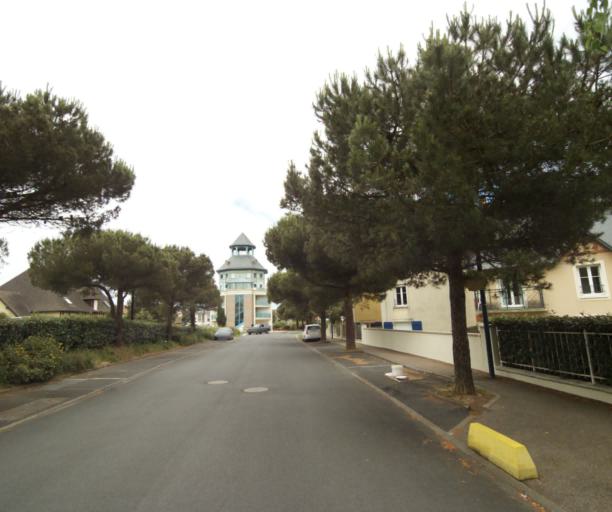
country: FR
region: Lower Normandy
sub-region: Departement du Calvados
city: Dives-sur-Mer
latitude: 49.2938
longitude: -0.1012
